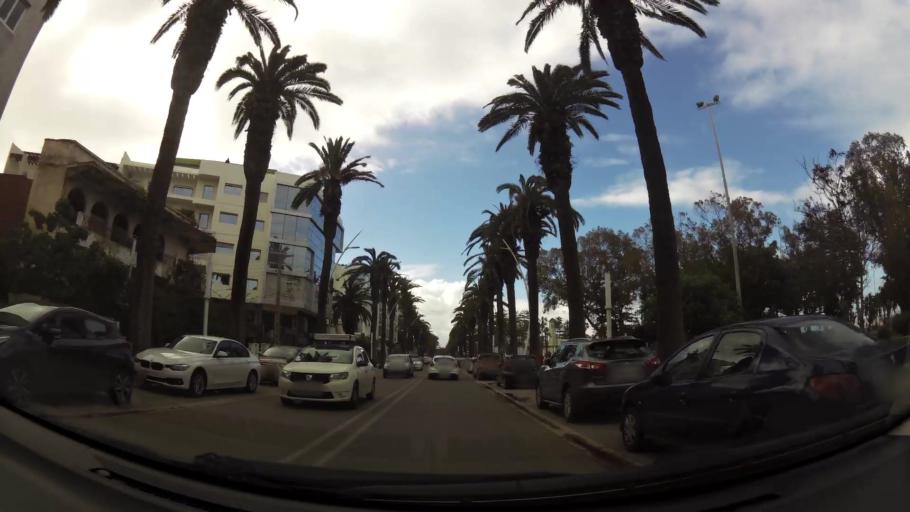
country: MA
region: Doukkala-Abda
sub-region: El-Jadida
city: El Jadida
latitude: 33.2466
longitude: -8.4966
